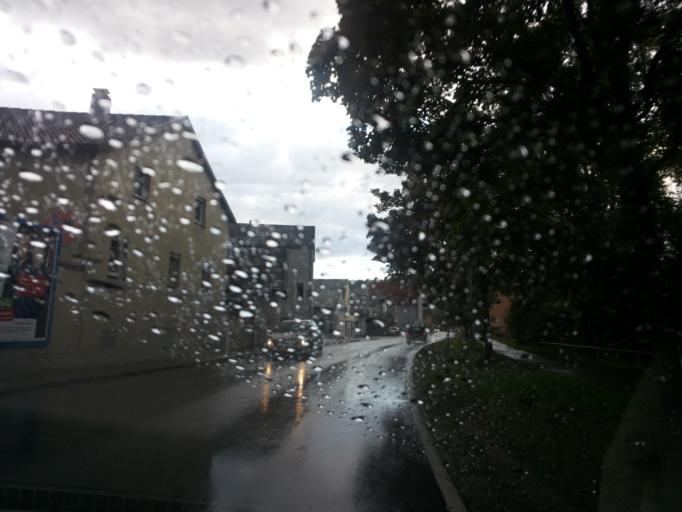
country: DE
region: Bavaria
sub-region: Upper Bavaria
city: Eichstaett
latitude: 48.8901
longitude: 11.1814
